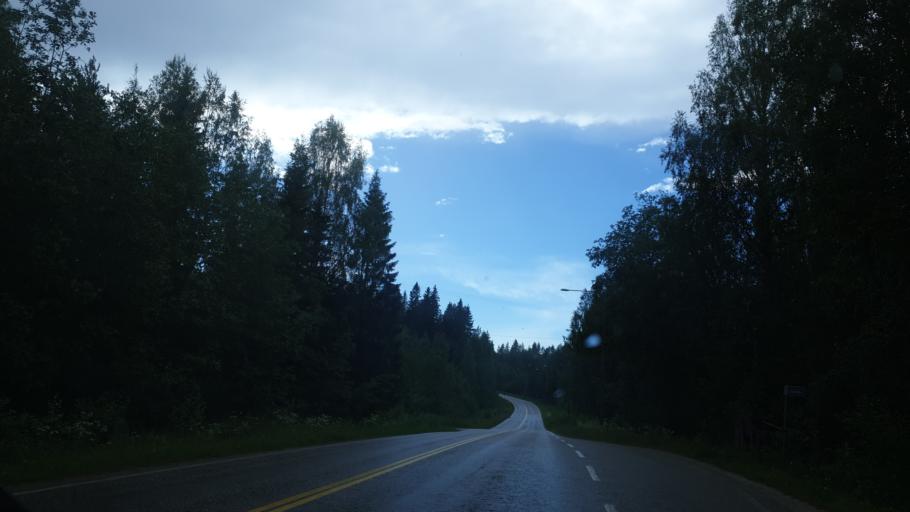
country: FI
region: Northern Savo
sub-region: Kuopio
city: Kuopio
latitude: 62.9128
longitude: 27.8756
